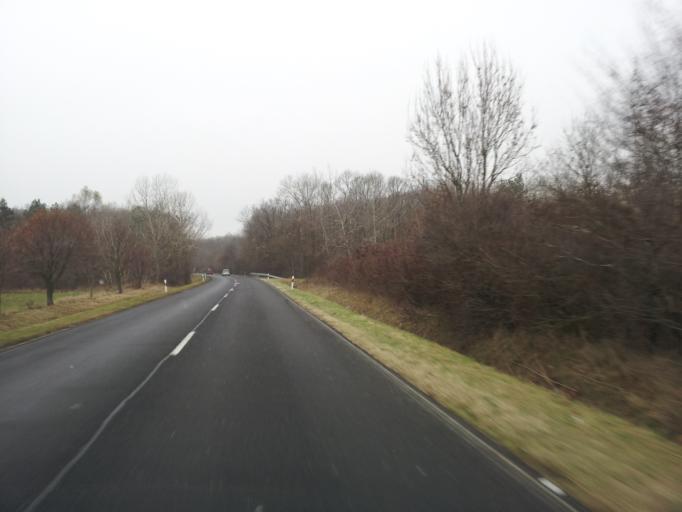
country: HU
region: Veszprem
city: Ajka
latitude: 47.1386
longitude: 17.5332
